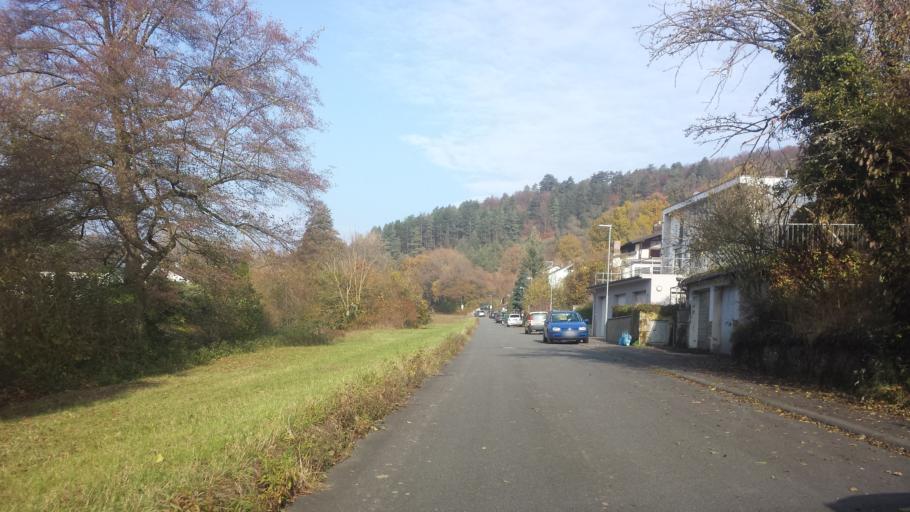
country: DE
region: Baden-Wuerttemberg
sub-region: Karlsruhe Region
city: Mosbach
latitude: 49.3548
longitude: 9.1302
